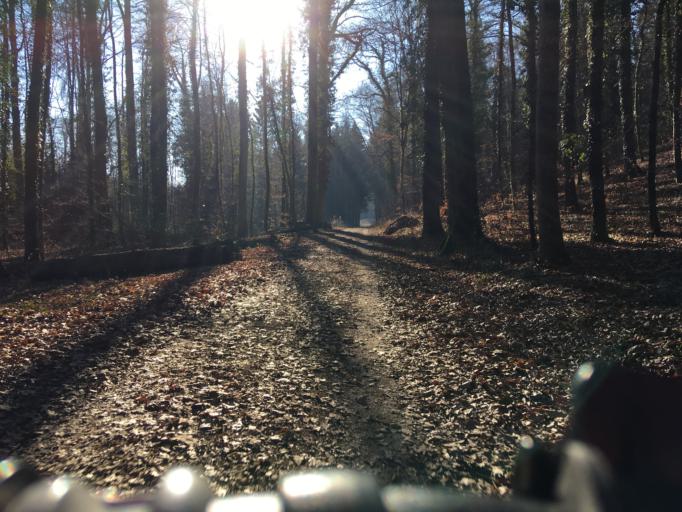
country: DE
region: Baden-Wuerttemberg
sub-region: Freiburg Region
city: Gottmadingen
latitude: 47.7453
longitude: 8.8046
